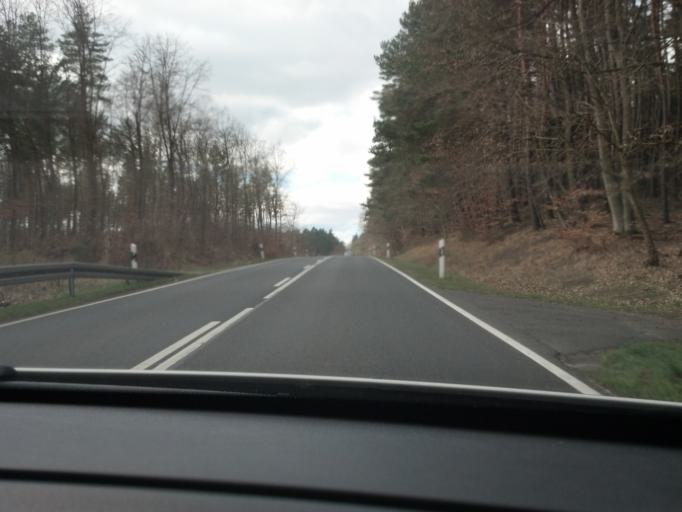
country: DE
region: Mecklenburg-Vorpommern
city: Carpin
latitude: 53.3663
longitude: 13.1985
